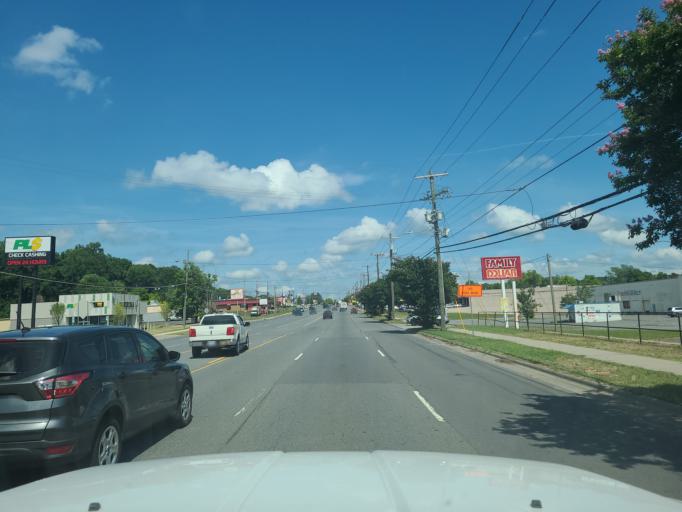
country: US
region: North Carolina
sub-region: Mecklenburg County
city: Charlotte
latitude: 35.2584
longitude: -80.7922
